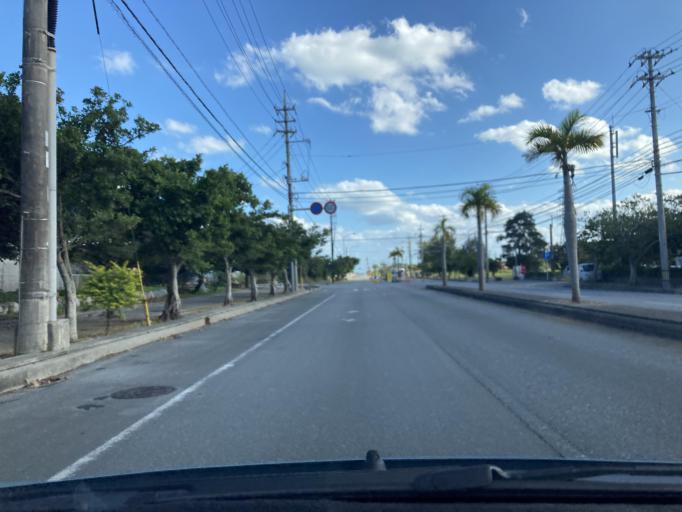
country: JP
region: Okinawa
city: Katsuren-haebaru
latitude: 26.3325
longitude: 127.8527
